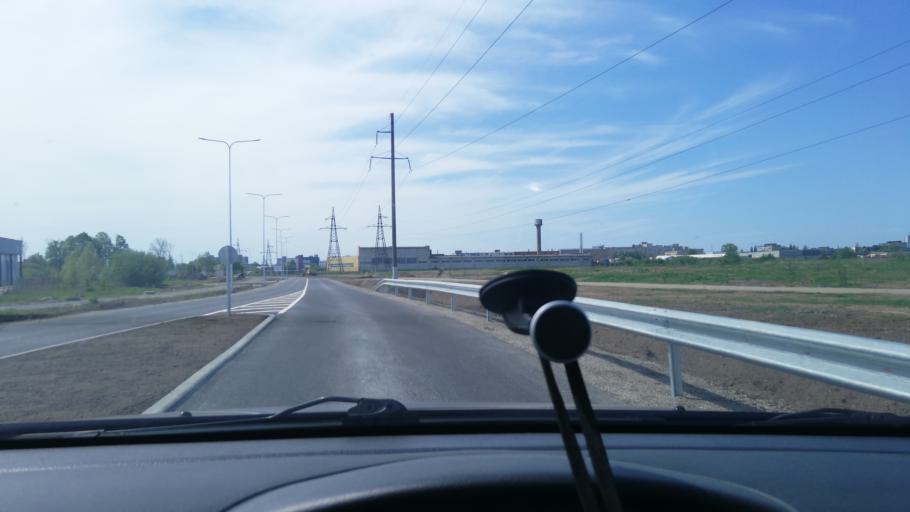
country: LT
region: Klaipedos apskritis
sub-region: Klaipeda
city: Klaipeda
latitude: 55.6855
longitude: 21.2011
